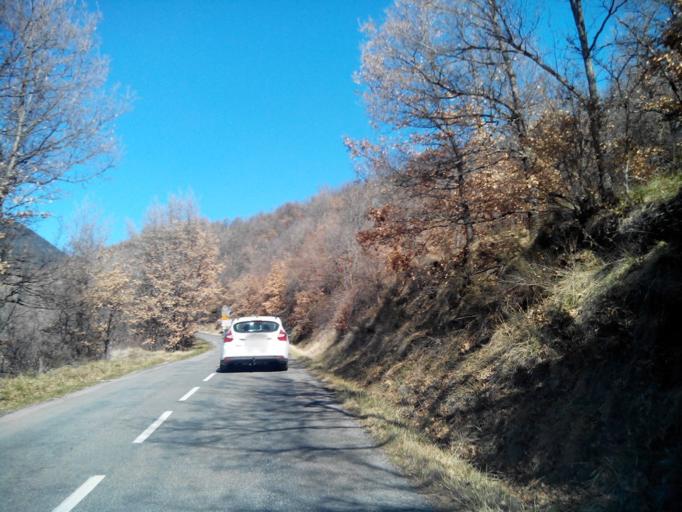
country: ES
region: Catalonia
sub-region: Provincia de Lleida
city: Lles de Cerdanya
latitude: 42.3831
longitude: 1.6834
